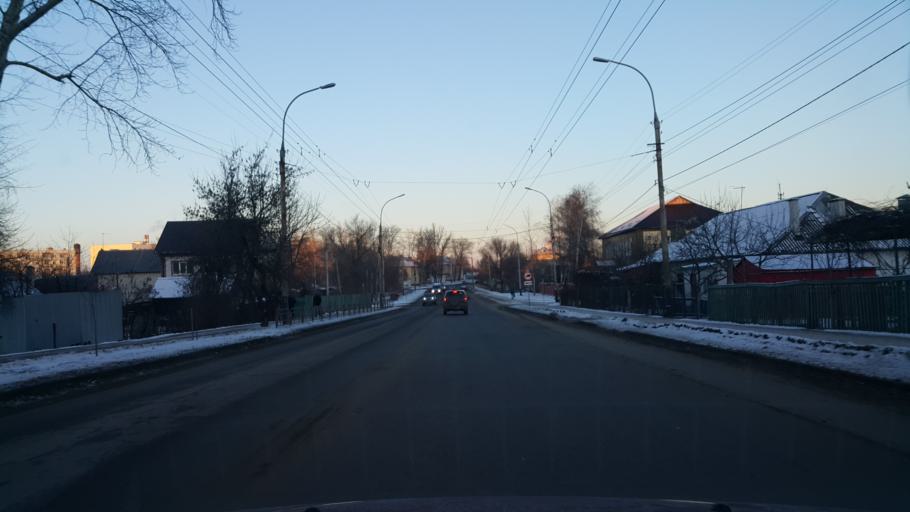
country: RU
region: Tambov
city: Pokrovo-Prigorodnoye
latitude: 52.7109
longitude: 41.3983
